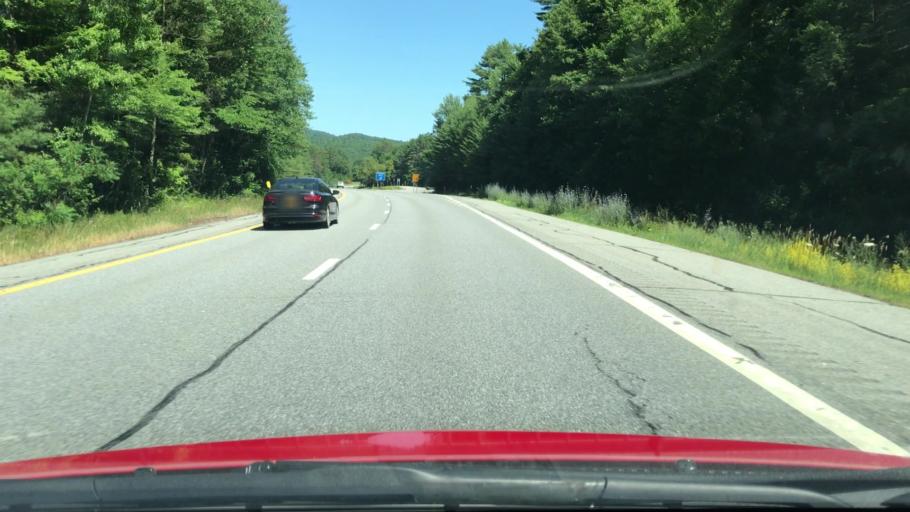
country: US
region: New York
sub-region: Warren County
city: Warrensburg
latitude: 43.5464
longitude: -73.7339
